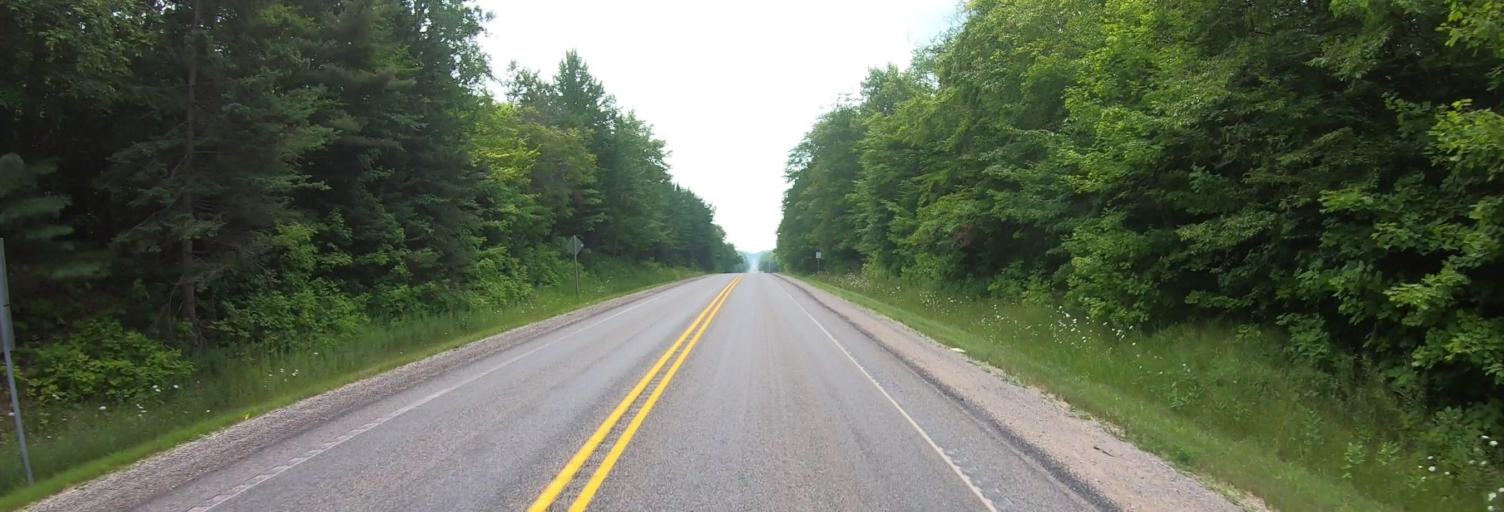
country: US
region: Michigan
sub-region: Alger County
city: Munising
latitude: 46.3752
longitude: -86.7017
